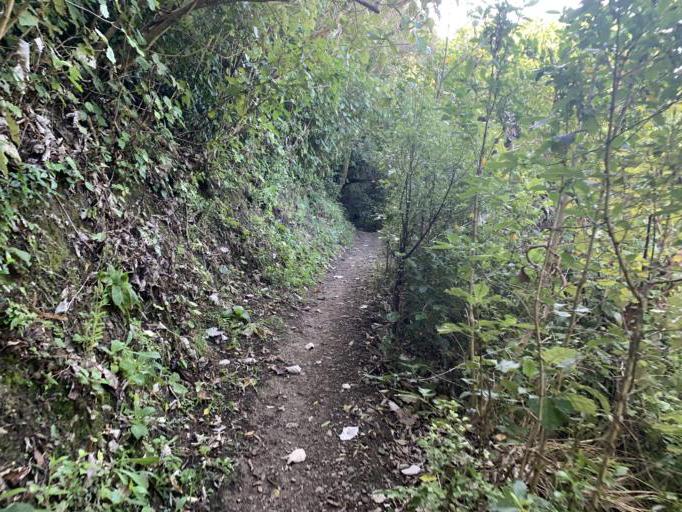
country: NZ
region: Wellington
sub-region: Wellington City
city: Brooklyn
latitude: -41.3004
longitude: 174.7532
